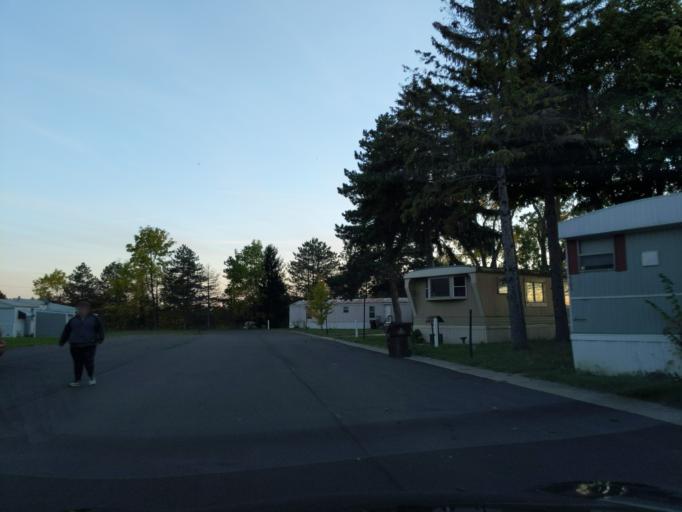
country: US
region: Michigan
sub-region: Ingham County
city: Edgemont Park
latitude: 42.7239
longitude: -84.5996
